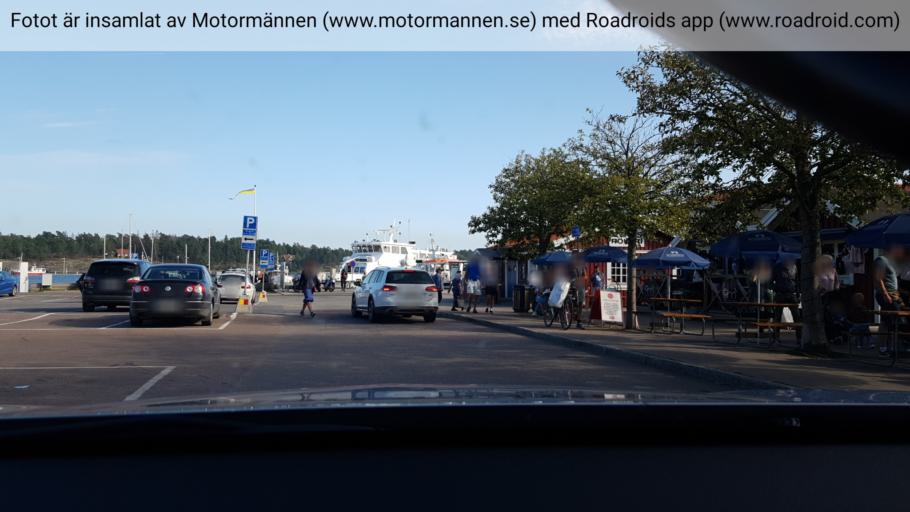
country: SE
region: Stockholm
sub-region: Nynashamns Kommun
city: Nynashamn
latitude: 58.9010
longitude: 17.9523
